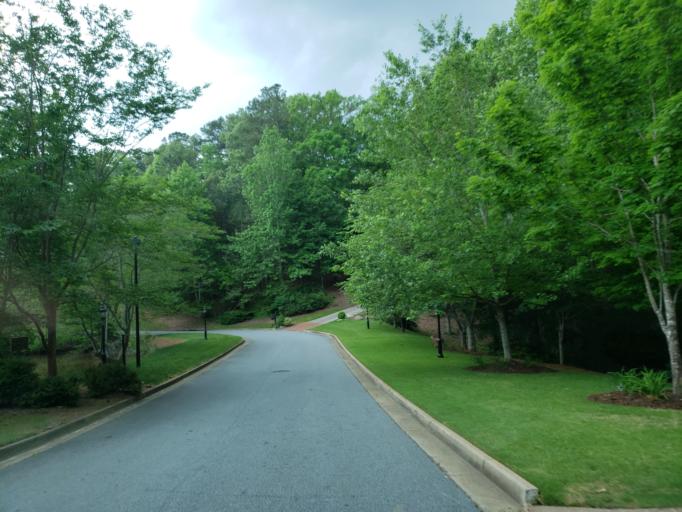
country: US
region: Georgia
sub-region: Cobb County
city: Marietta
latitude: 33.9579
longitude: -84.5771
